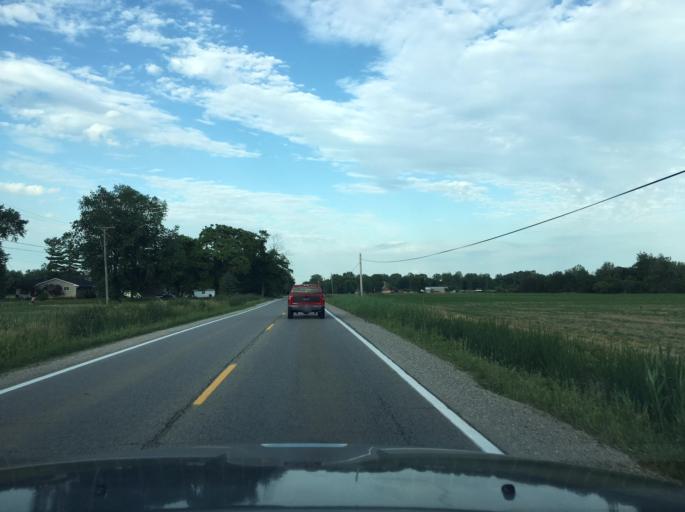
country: US
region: Michigan
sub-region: Macomb County
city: New Haven
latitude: 42.7170
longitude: -82.9130
